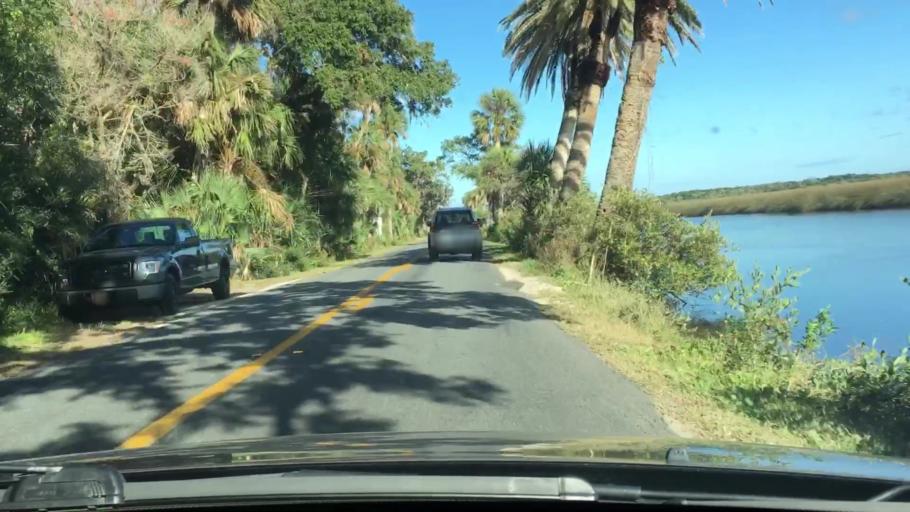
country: US
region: Florida
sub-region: Volusia County
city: Ormond-by-the-Sea
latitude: 29.4020
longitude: -81.1131
